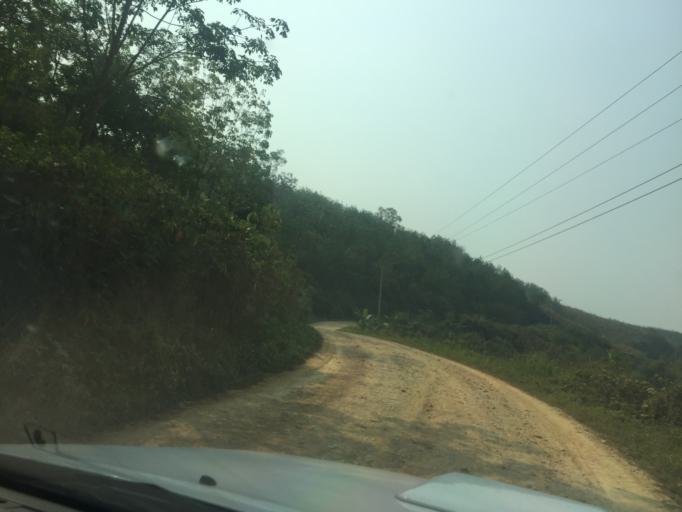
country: TH
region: Phayao
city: Phu Sang
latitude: 19.6531
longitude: 100.5270
